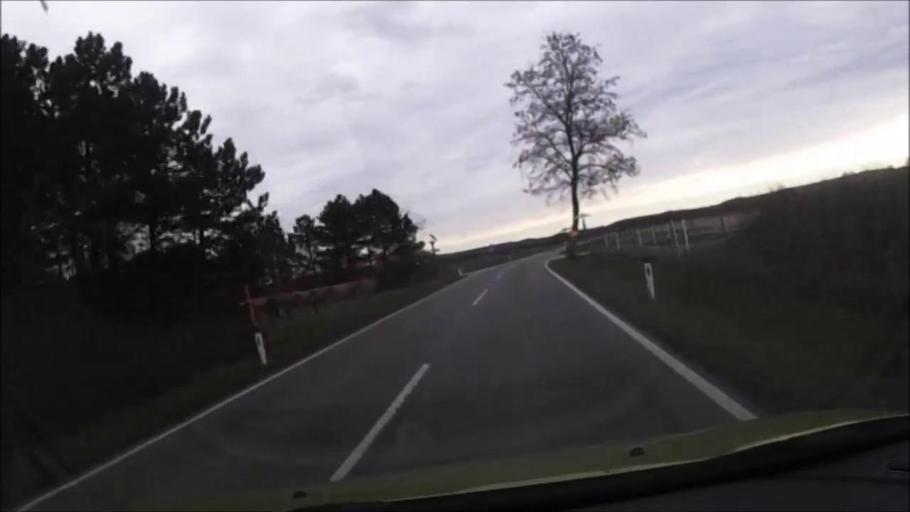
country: AT
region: Burgenland
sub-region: Eisenstadt-Umgebung
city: Leithaprodersdorf
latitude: 47.9498
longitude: 16.4528
